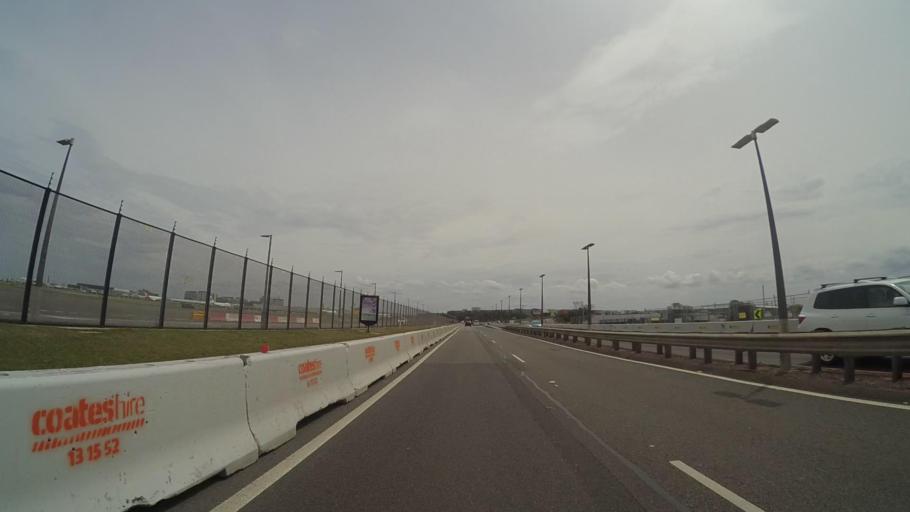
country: AU
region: New South Wales
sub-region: Botany Bay
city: Mascot
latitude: -33.9267
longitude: 151.1742
